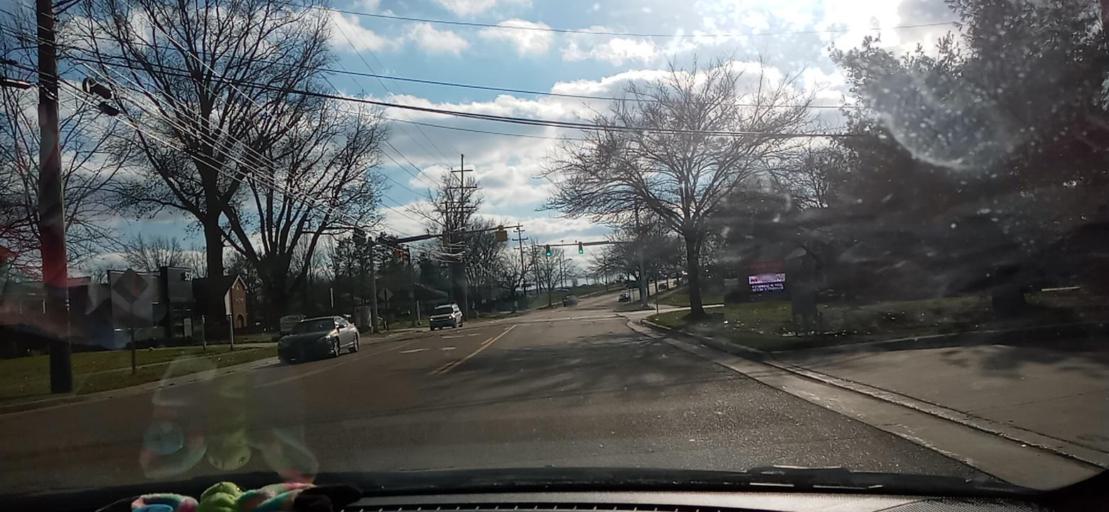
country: US
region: Ohio
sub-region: Summit County
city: Fairlawn
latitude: 41.1023
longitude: -81.5863
